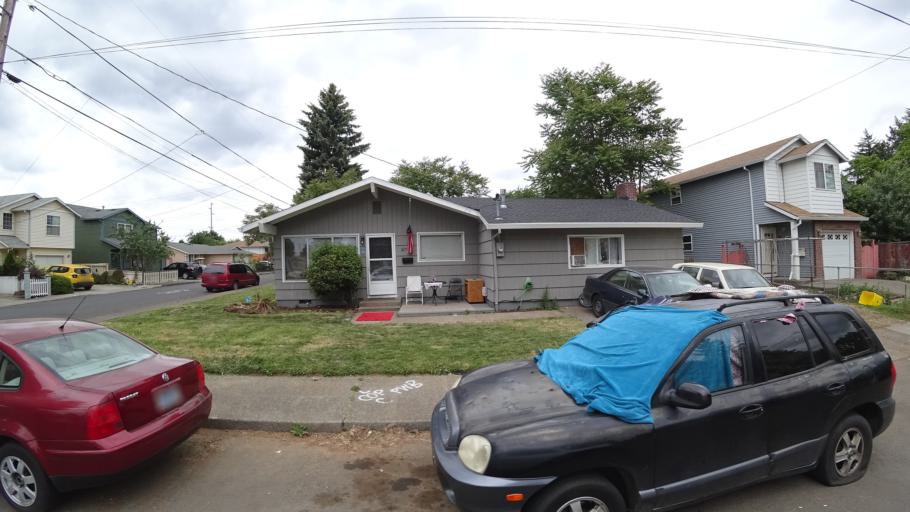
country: US
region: Oregon
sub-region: Multnomah County
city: Lents
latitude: 45.4891
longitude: -122.5731
